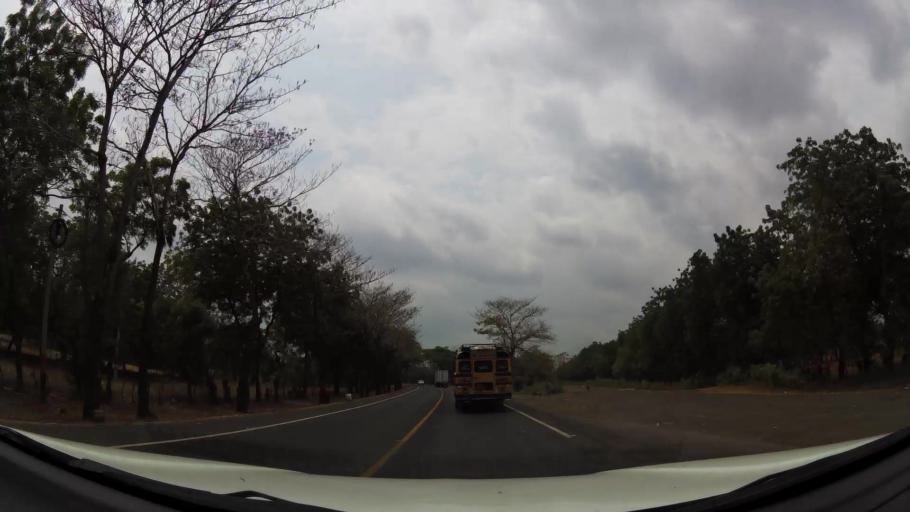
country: NI
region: Leon
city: Telica
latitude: 12.5094
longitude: -86.8601
